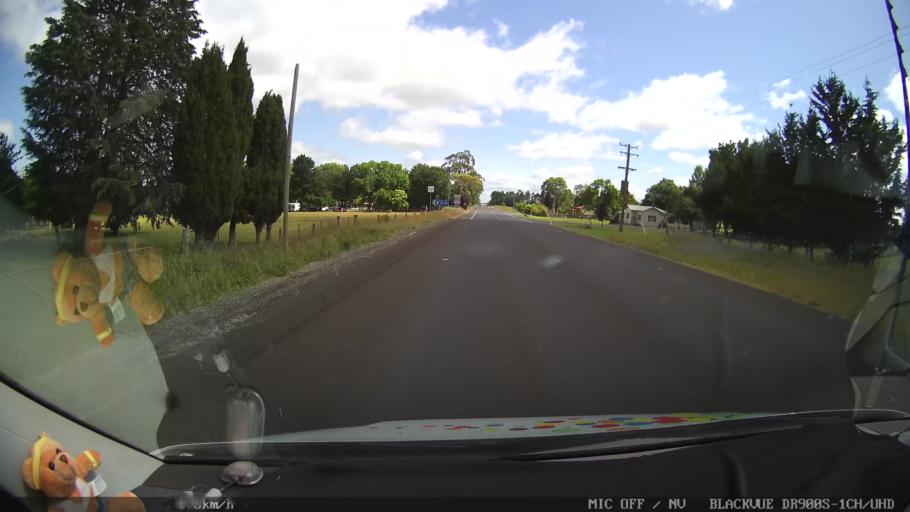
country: AU
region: New South Wales
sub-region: Glen Innes Severn
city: Glen Innes
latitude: -29.7731
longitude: 151.7316
